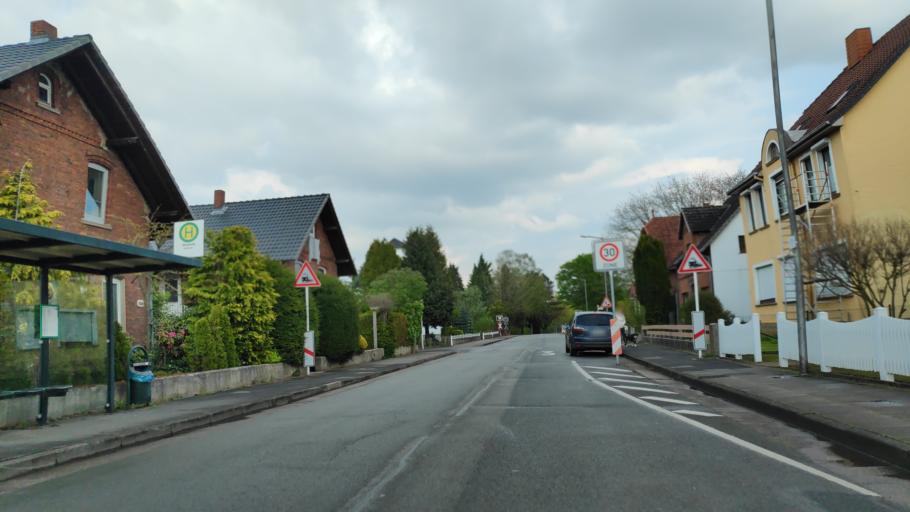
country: DE
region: North Rhine-Westphalia
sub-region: Regierungsbezirk Detmold
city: Minden
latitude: 52.2907
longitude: 8.9582
